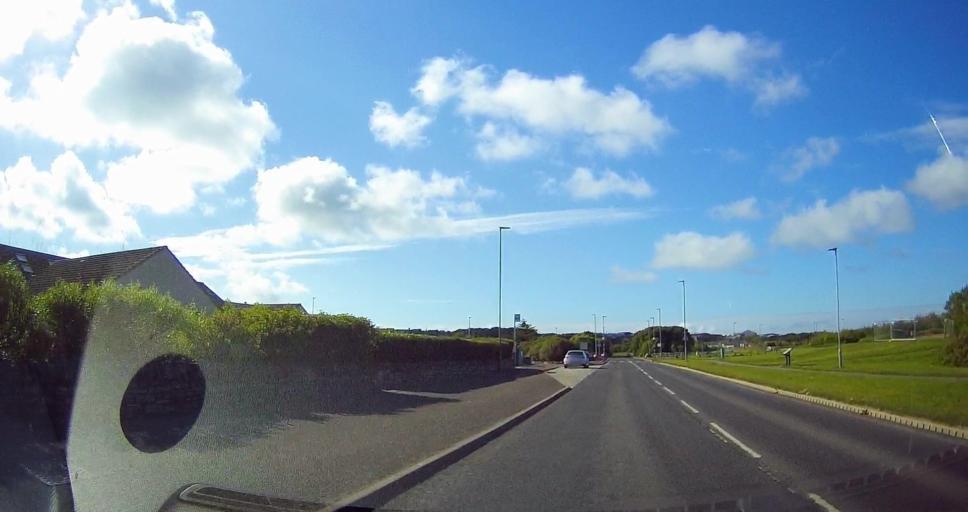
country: GB
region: Scotland
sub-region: Orkney Islands
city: Orkney
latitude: 58.9816
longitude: -2.9688
